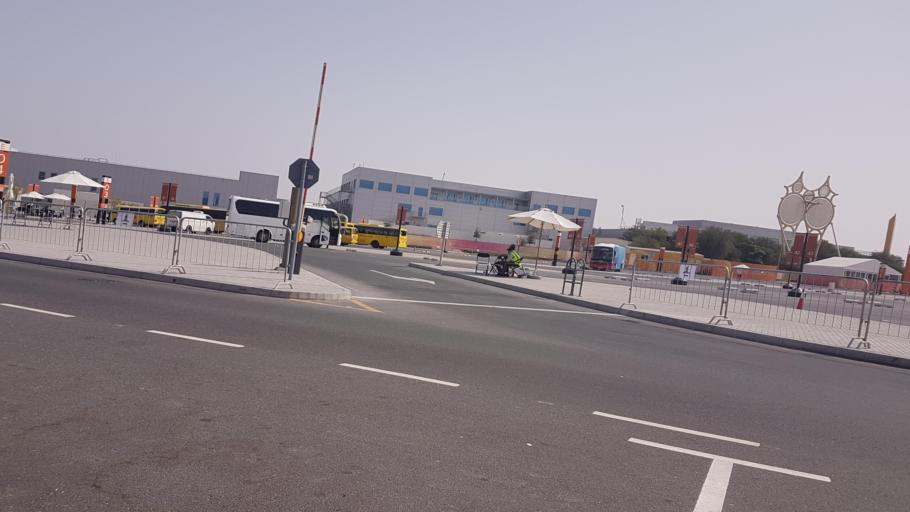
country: AE
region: Dubai
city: Dubai
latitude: 24.9660
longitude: 55.1564
